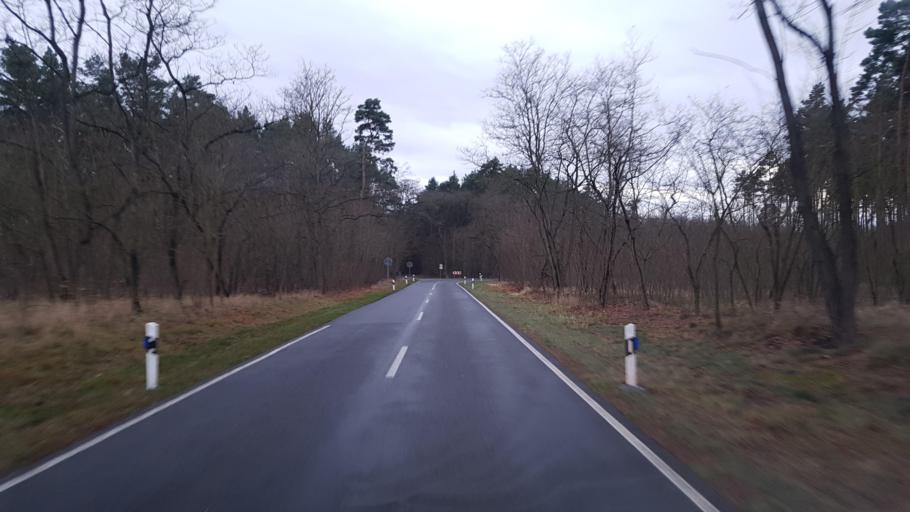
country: DE
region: Brandenburg
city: Schlepzig
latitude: 52.0564
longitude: 14.0174
